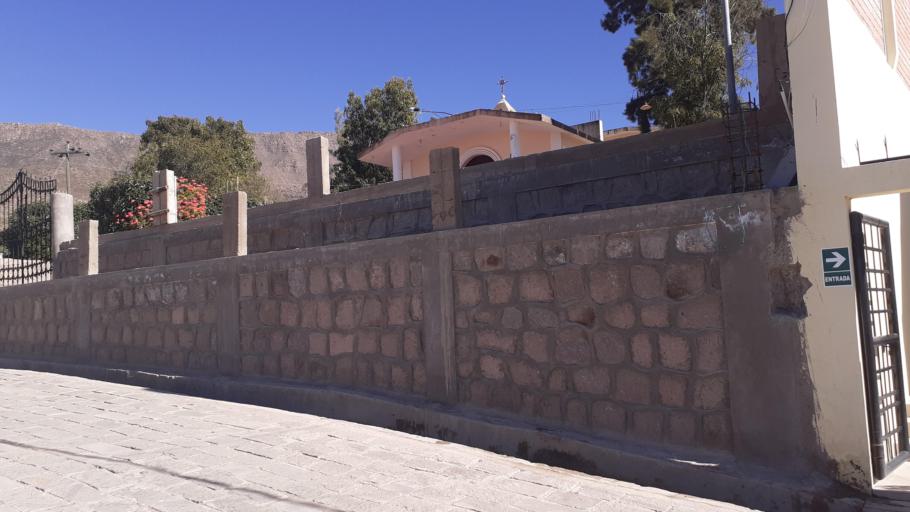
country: PE
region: Arequipa
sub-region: Provincia de Condesuyos
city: Chuquibamba
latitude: -15.8354
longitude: -72.6541
